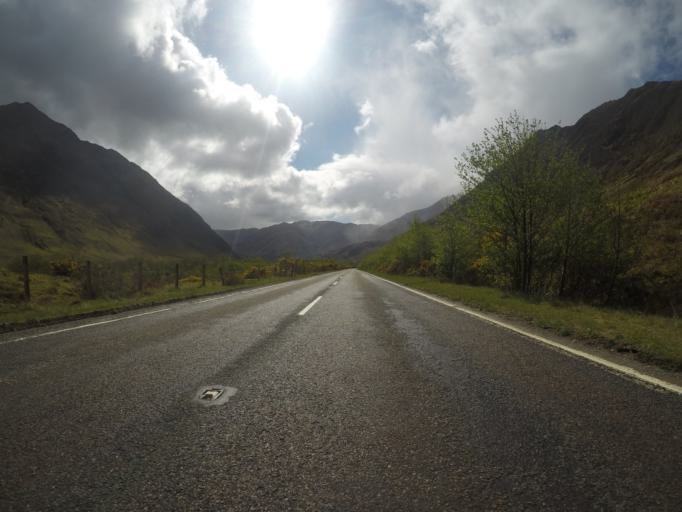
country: GB
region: Scotland
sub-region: Highland
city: Fort William
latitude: 57.1904
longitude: -5.3857
